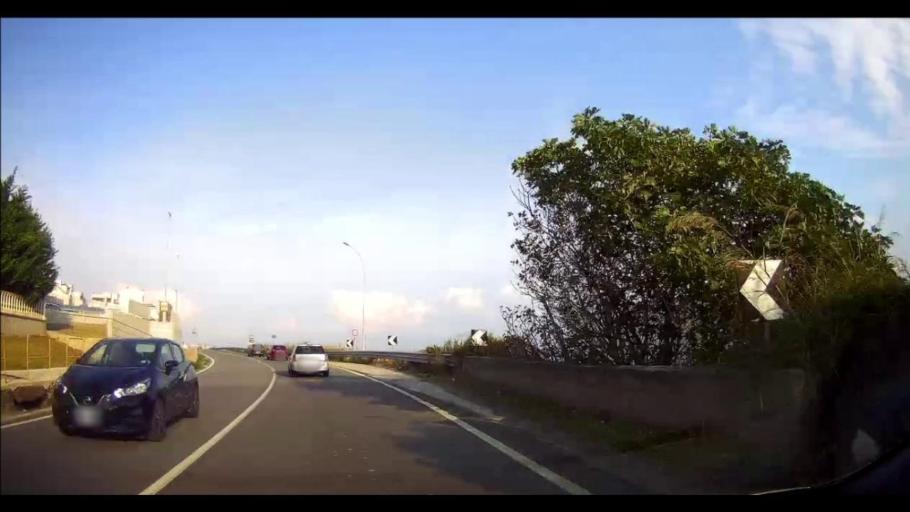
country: IT
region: Calabria
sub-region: Provincia di Cosenza
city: Cariati
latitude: 39.5072
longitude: 16.9358
